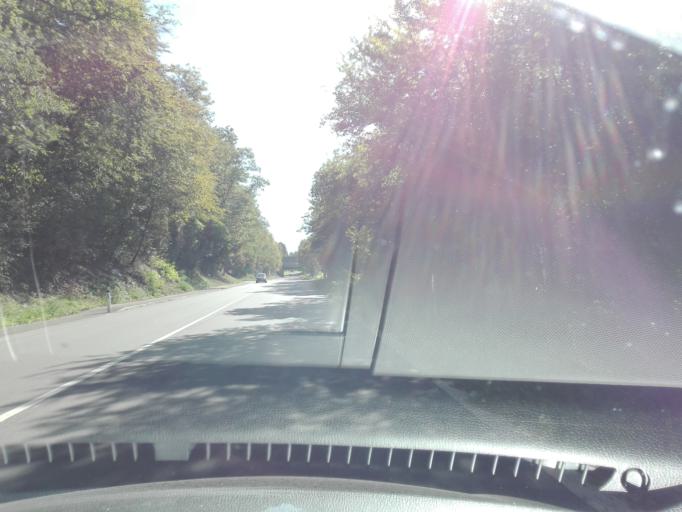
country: AT
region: Upper Austria
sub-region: Politischer Bezirk Linz-Land
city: Sankt Florian
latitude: 48.2384
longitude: 14.3365
